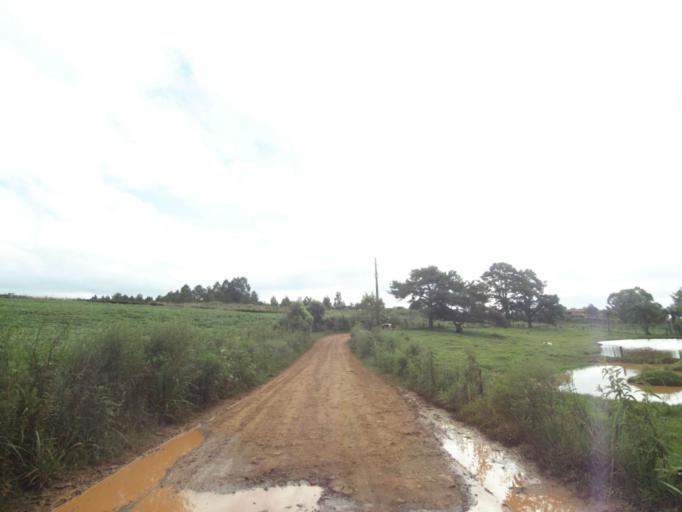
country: BR
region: Rio Grande do Sul
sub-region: Lagoa Vermelha
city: Lagoa Vermelha
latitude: -28.2015
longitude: -51.5152
